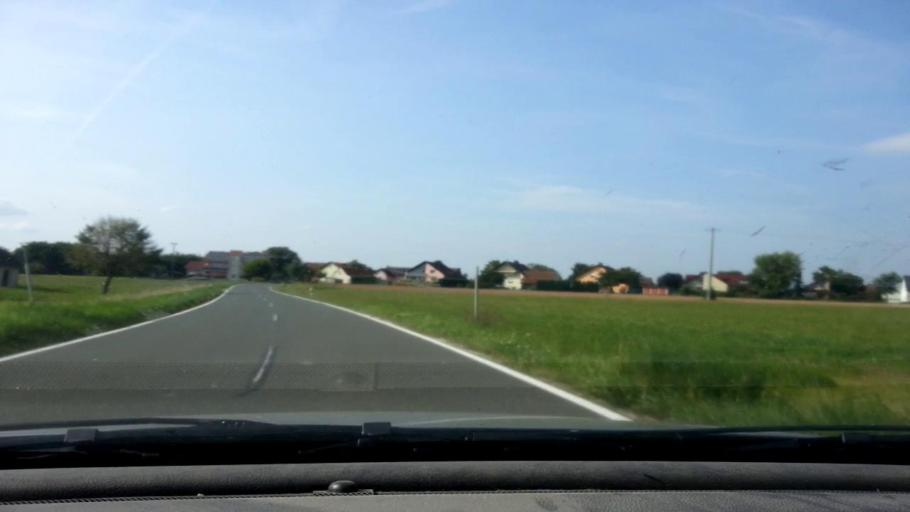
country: DE
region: Bavaria
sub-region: Upper Franconia
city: Zapfendorf
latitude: 49.9860
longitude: 10.9541
